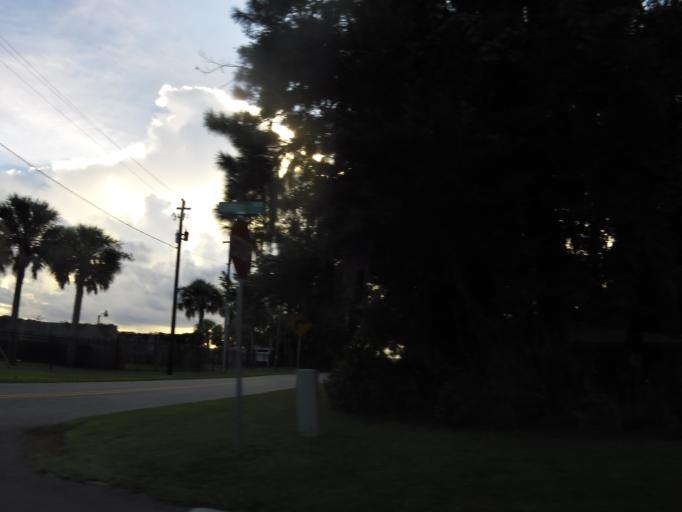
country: US
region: Georgia
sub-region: Camden County
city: St. Marys
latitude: 30.7339
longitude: -81.5582
